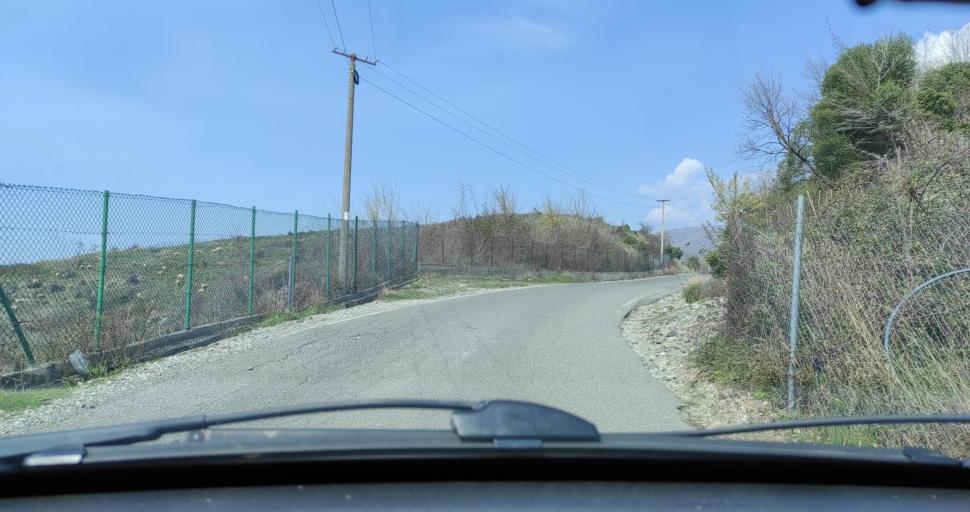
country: AL
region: Lezhe
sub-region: Rrethi i Lezhes
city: Kallmeti i Madh
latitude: 41.8626
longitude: 19.6985
